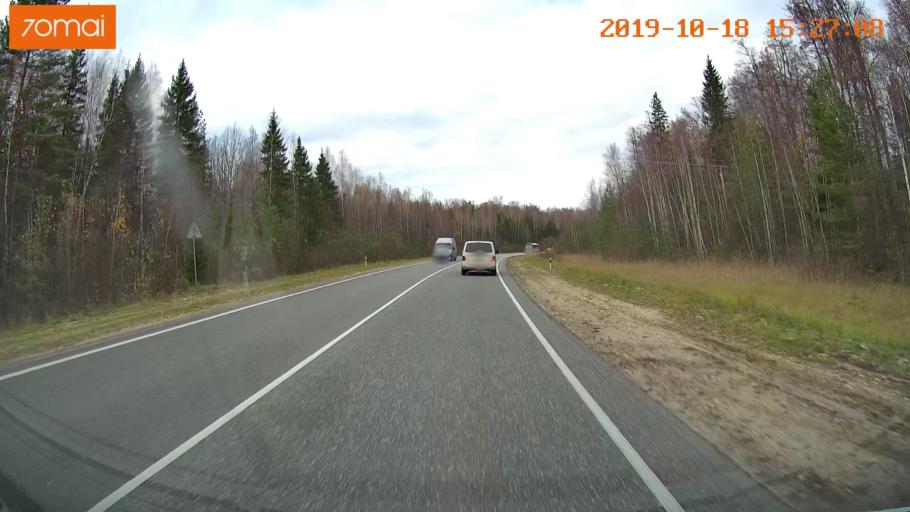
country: RU
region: Vladimir
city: Anopino
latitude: 55.7496
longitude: 40.6725
